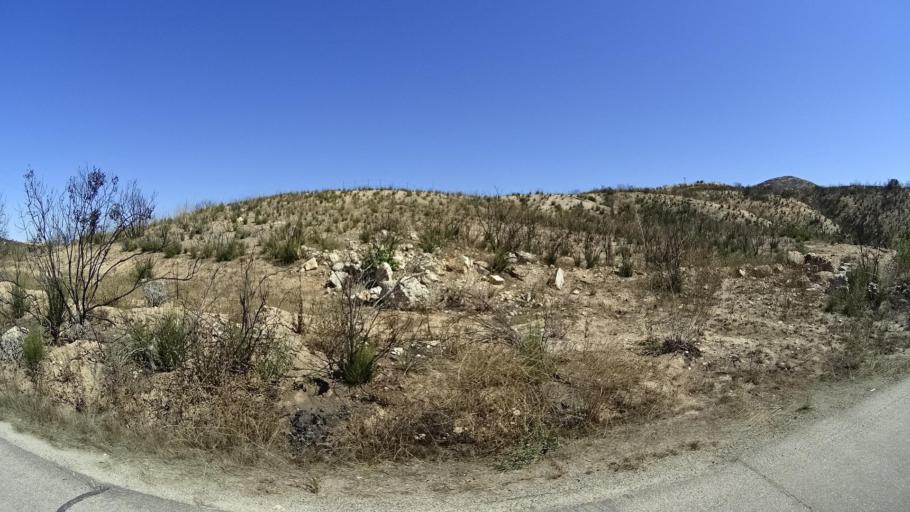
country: US
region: California
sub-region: San Diego County
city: Alpine
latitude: 32.7721
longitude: -116.7632
